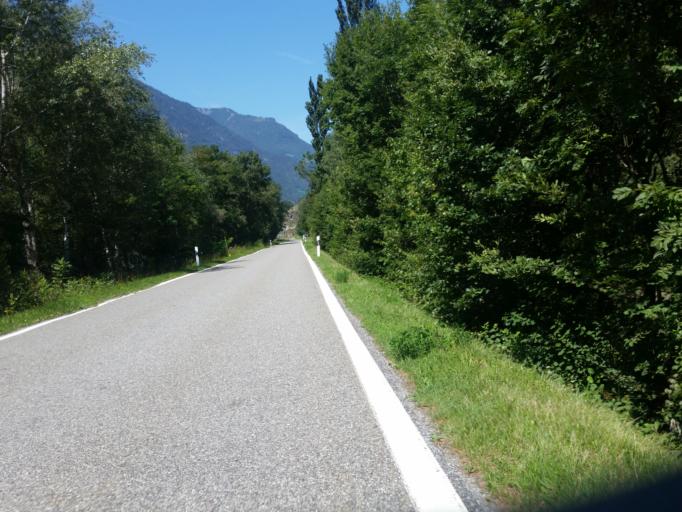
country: CH
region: Valais
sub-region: Saint-Maurice District
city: Vernayaz
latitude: 46.1380
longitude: 7.0526
